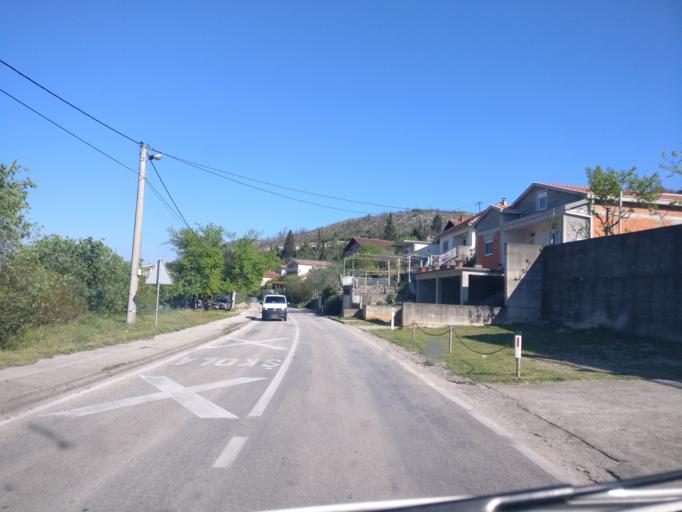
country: BA
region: Federation of Bosnia and Herzegovina
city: Capljina
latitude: 43.1340
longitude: 17.6752
